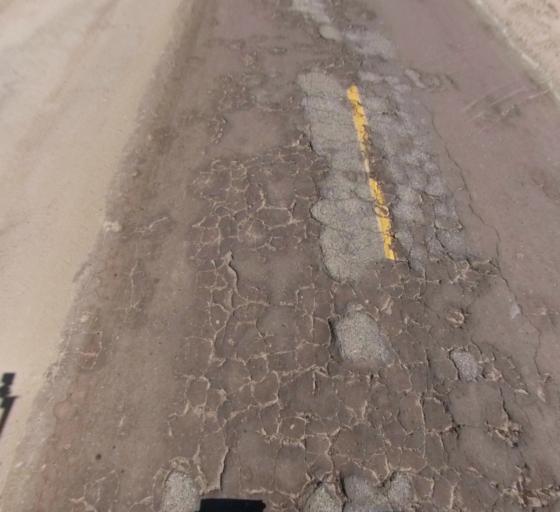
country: US
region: California
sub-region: Fresno County
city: Biola
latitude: 36.8425
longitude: -120.0373
